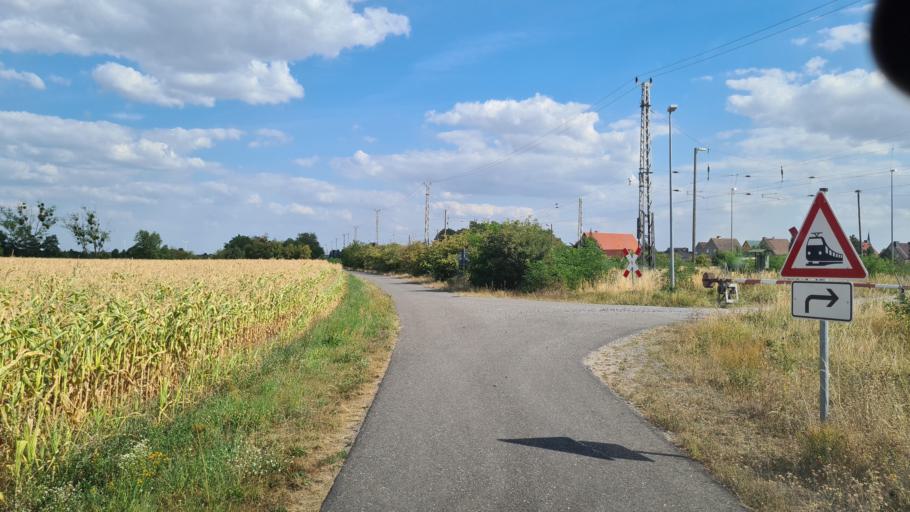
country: DE
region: Saxony-Anhalt
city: Elster
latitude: 51.8356
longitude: 12.8175
